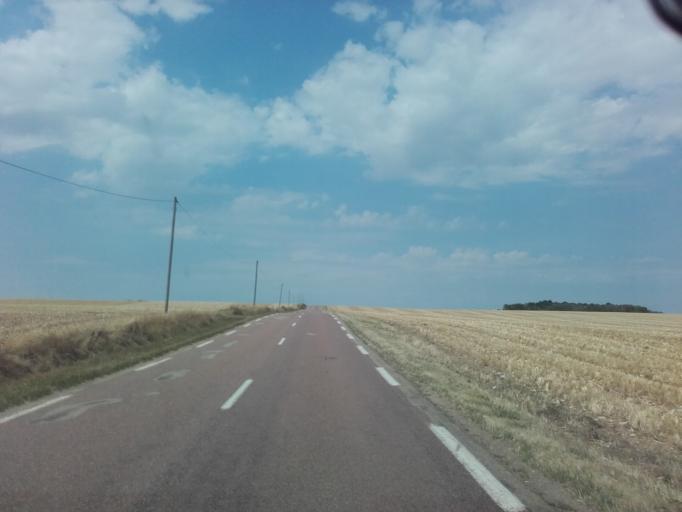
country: FR
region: Bourgogne
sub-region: Departement de l'Yonne
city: Joux-la-Ville
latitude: 47.6813
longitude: 3.8713
